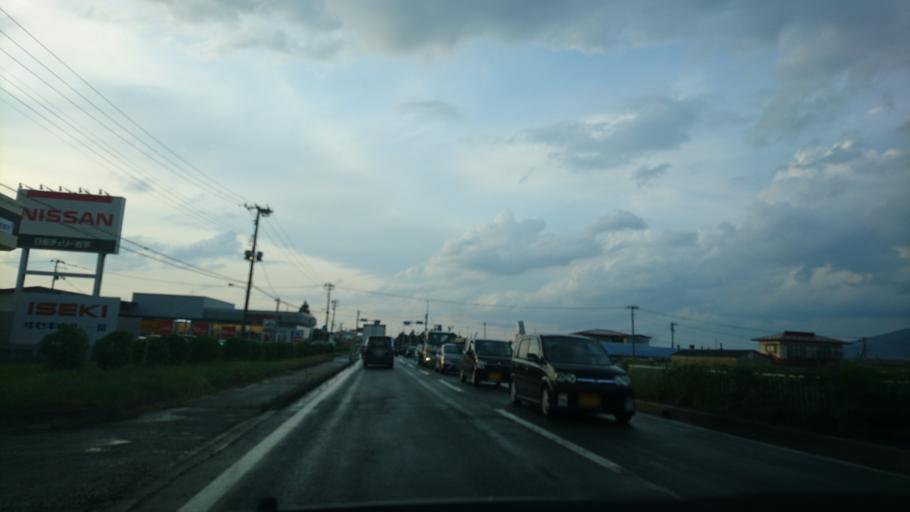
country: JP
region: Iwate
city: Ichinoseki
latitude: 38.9651
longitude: 141.1204
